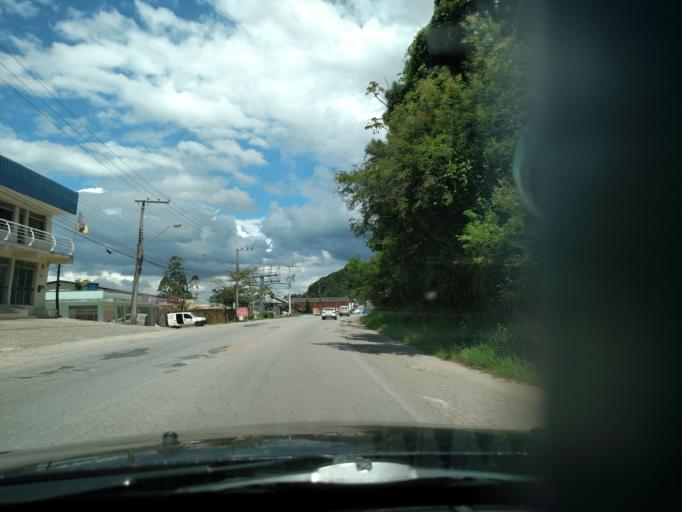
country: BR
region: Santa Catarina
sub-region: Gaspar
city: Gaspar
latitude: -26.9009
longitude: -48.9920
